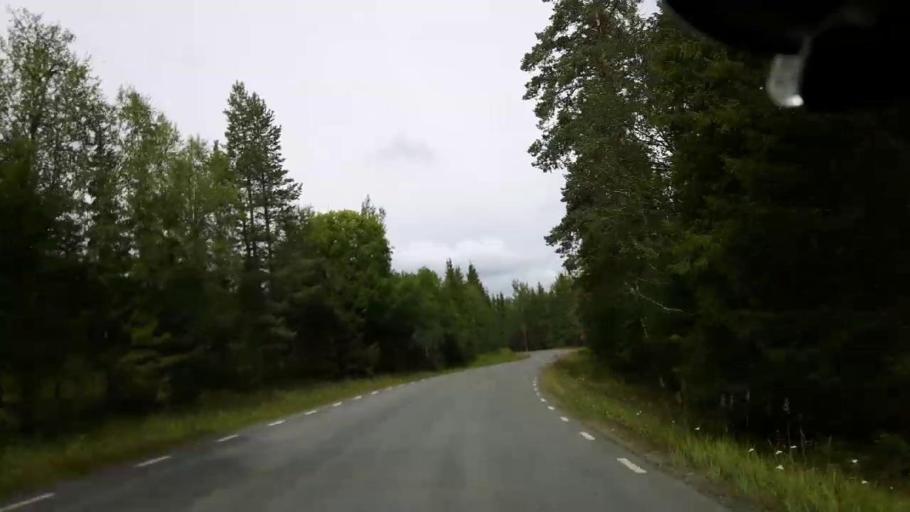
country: SE
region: Jaemtland
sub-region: Krokoms Kommun
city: Valla
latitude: 63.4718
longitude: 14.0073
